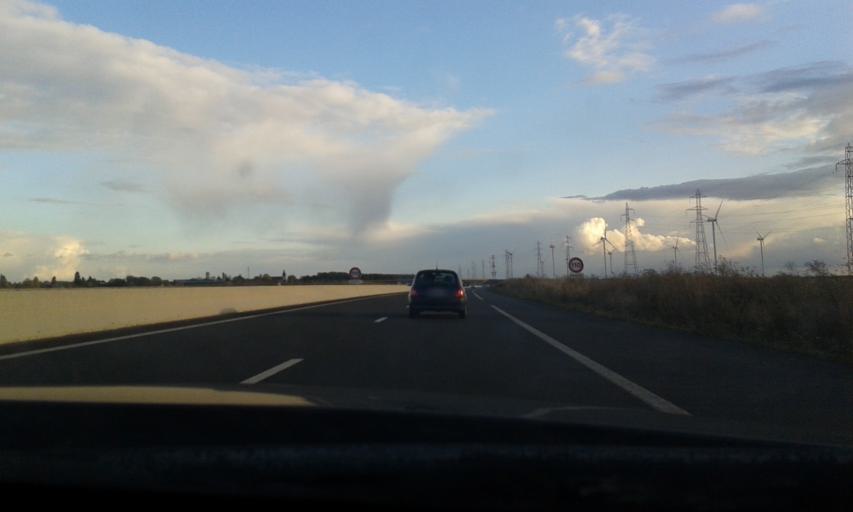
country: FR
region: Centre
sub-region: Departement d'Eure-et-Loir
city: Voves
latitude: 48.3352
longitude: 1.6426
